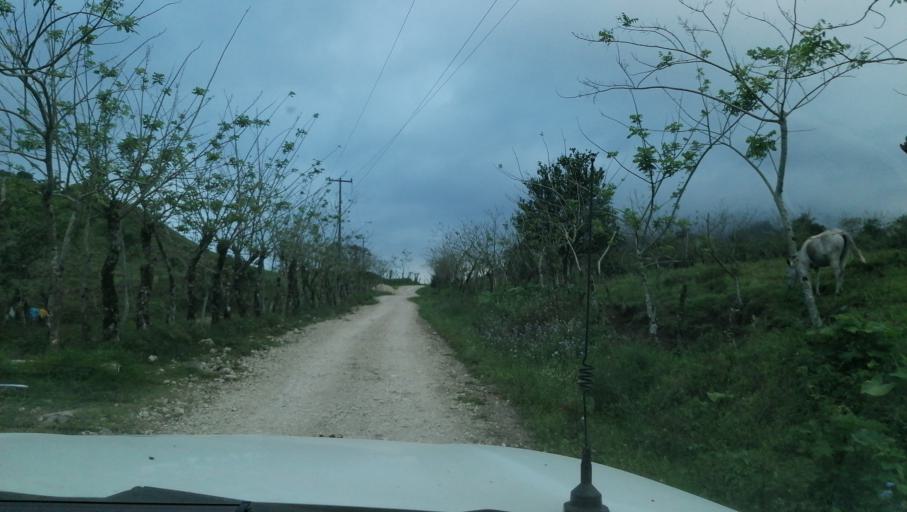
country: MX
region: Chiapas
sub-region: Francisco Leon
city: San Miguel la Sardina
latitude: 17.2889
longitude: -93.2700
